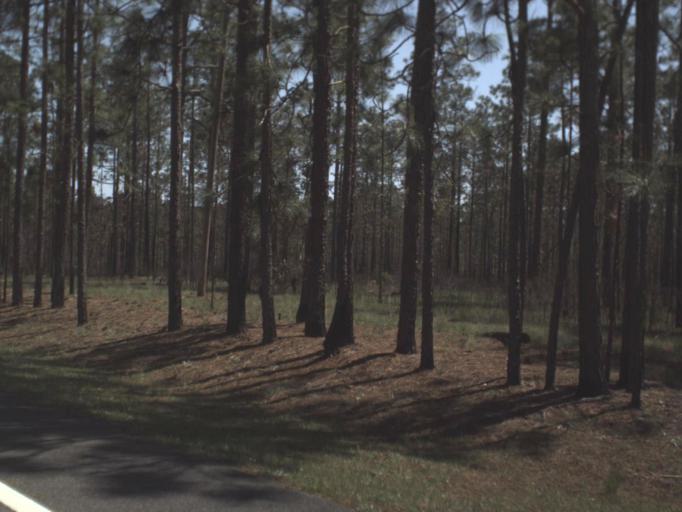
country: US
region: Florida
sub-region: Santa Rosa County
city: Point Baker
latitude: 30.8725
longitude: -86.9356
